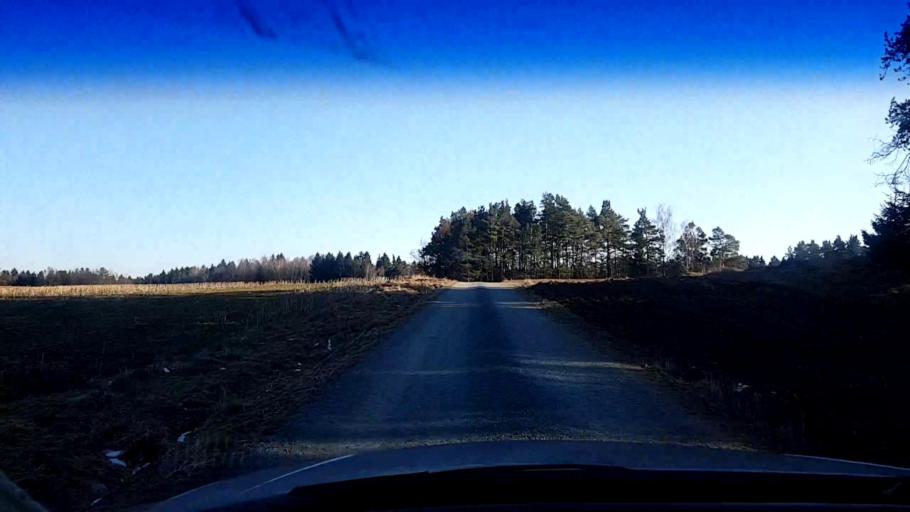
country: DE
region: Bavaria
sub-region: Upper Franconia
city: Aufsess
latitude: 49.9184
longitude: 11.2036
